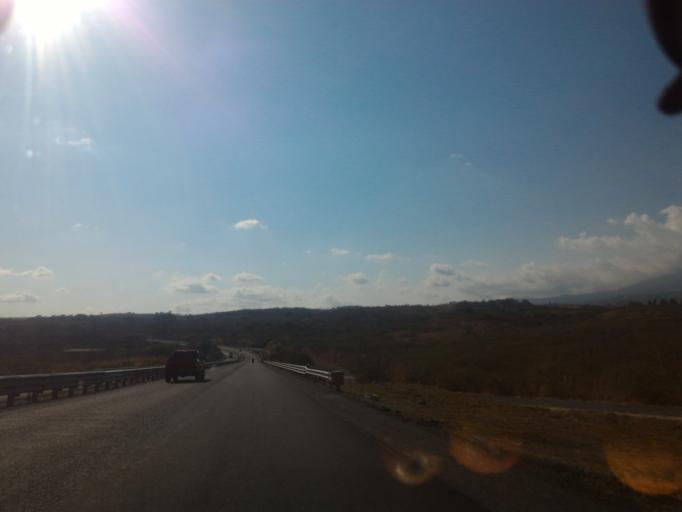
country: MX
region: Jalisco
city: Tonila
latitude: 19.4248
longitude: -103.5078
